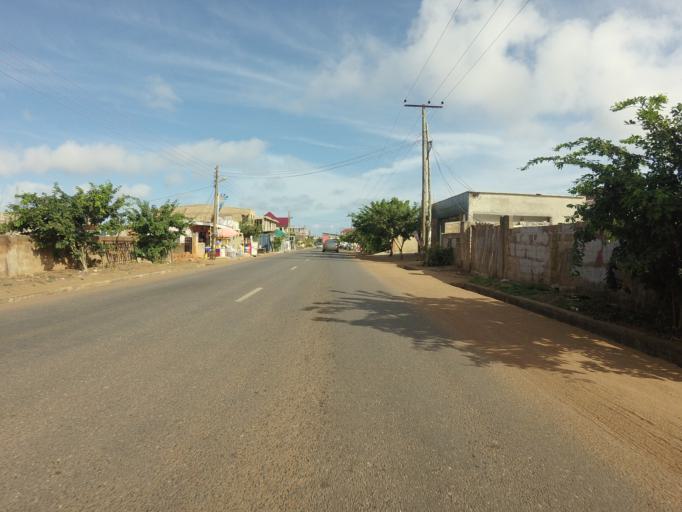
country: GH
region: Greater Accra
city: Teshi Old Town
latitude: 5.5791
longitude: -0.1407
